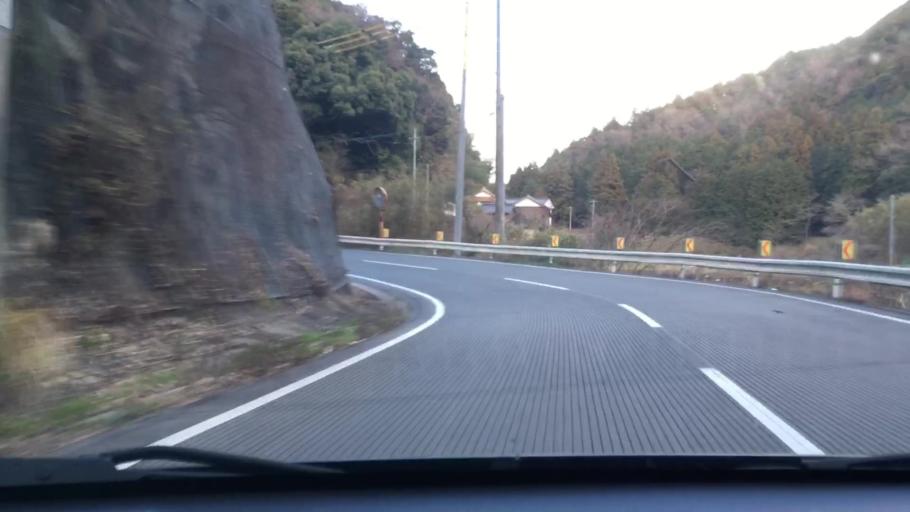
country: JP
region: Oita
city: Bungo-Takada-shi
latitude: 33.4631
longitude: 131.3890
